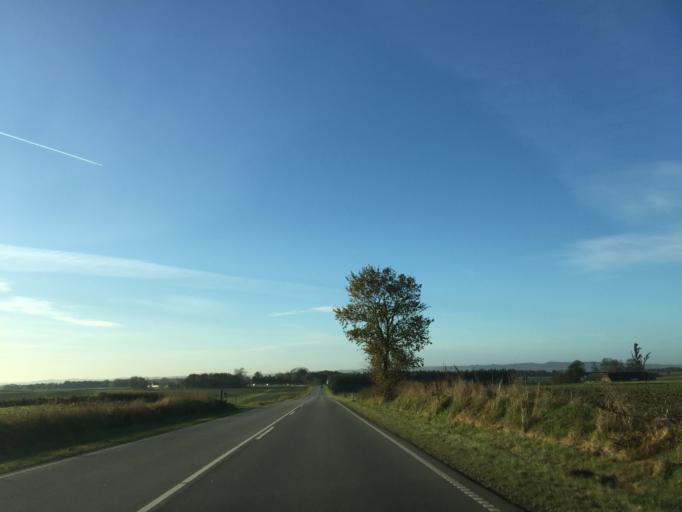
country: DK
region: Central Jutland
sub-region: Skanderborg Kommune
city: Skanderborg
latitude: 56.0754
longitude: 9.8971
